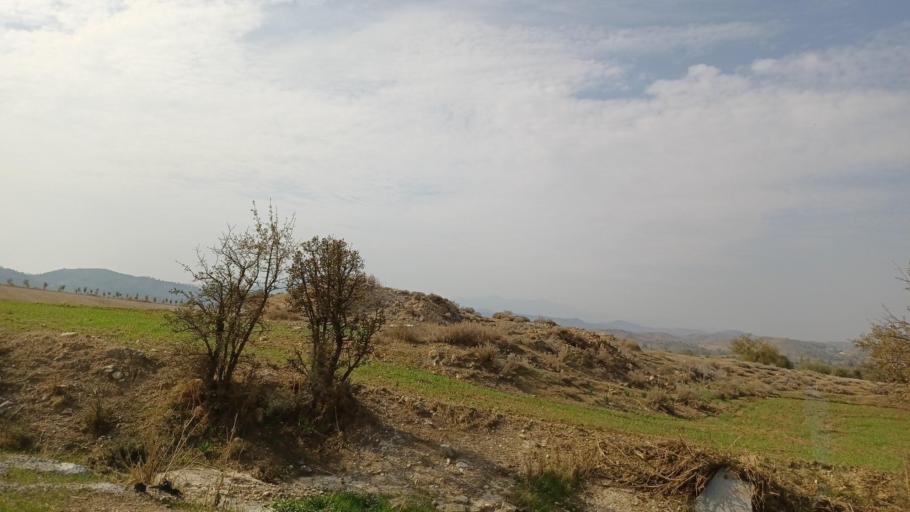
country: CY
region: Lefkosia
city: Lympia
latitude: 34.9812
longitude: 33.4554
